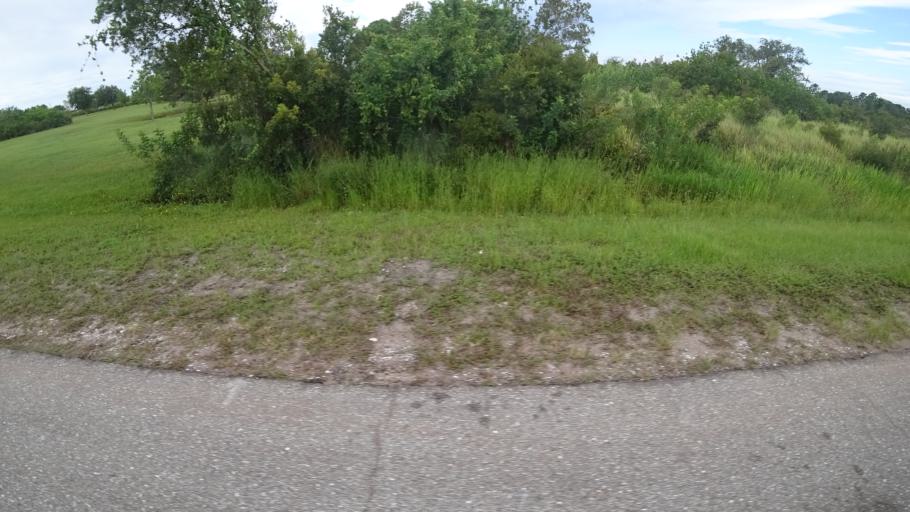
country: US
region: Florida
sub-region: Sarasota County
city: The Meadows
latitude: 27.4257
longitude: -82.2832
